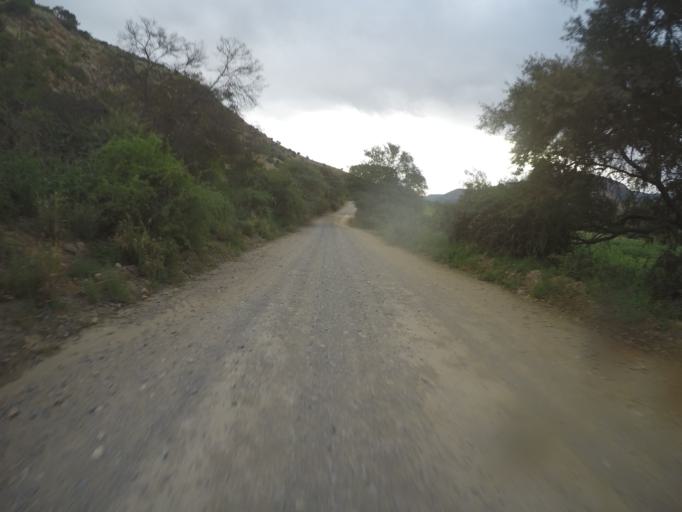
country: ZA
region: Eastern Cape
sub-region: Cacadu District Municipality
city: Willowmore
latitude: -33.5251
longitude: 23.8477
